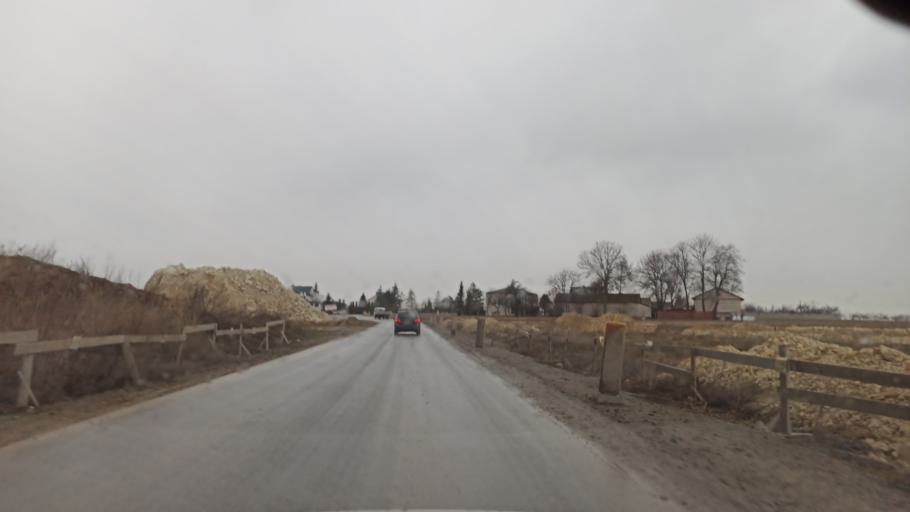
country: PL
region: Lublin Voivodeship
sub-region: Powiat lubelski
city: Niedrzwica Duza
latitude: 51.1032
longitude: 22.4067
